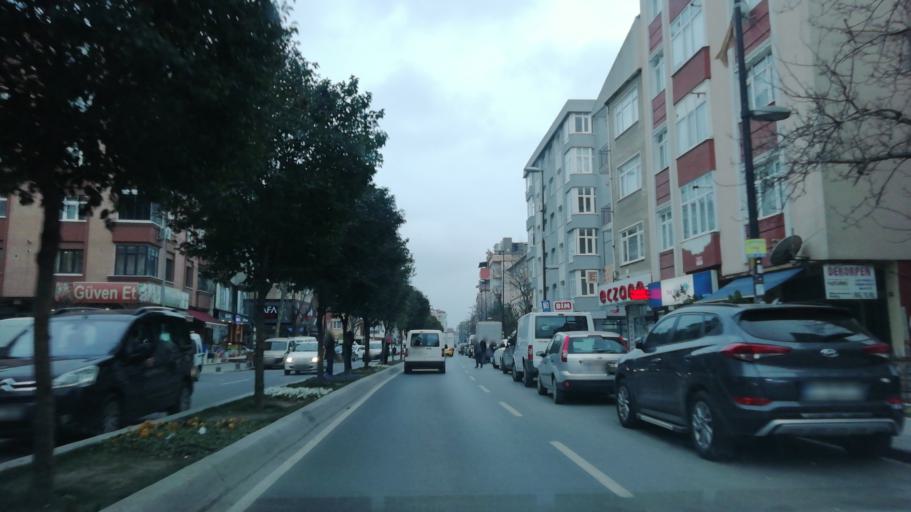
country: TR
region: Istanbul
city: Bahcelievler
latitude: 41.0089
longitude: 28.8499
